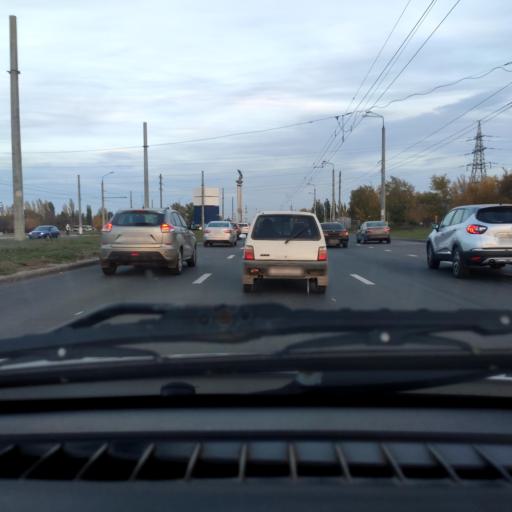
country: RU
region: Samara
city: Tol'yatti
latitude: 53.5536
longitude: 49.2835
